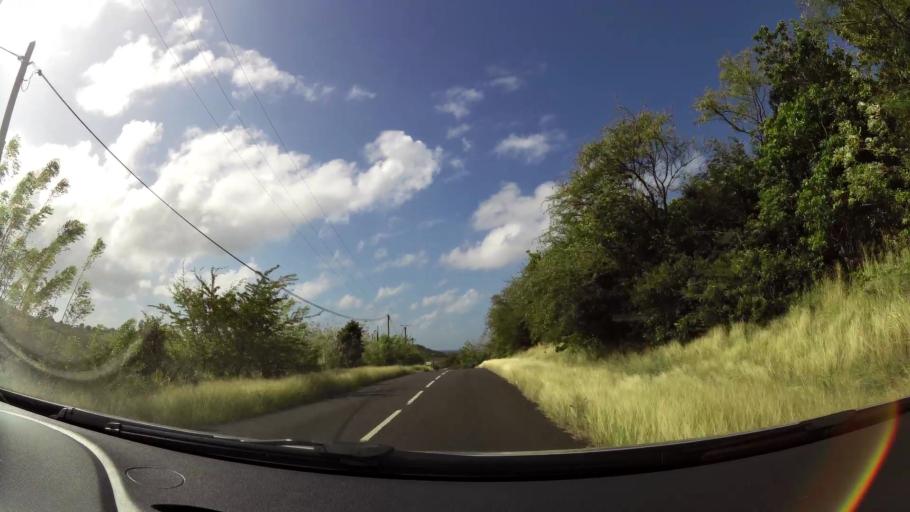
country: MQ
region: Martinique
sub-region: Martinique
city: Le Marin
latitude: 14.4214
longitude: -60.8763
